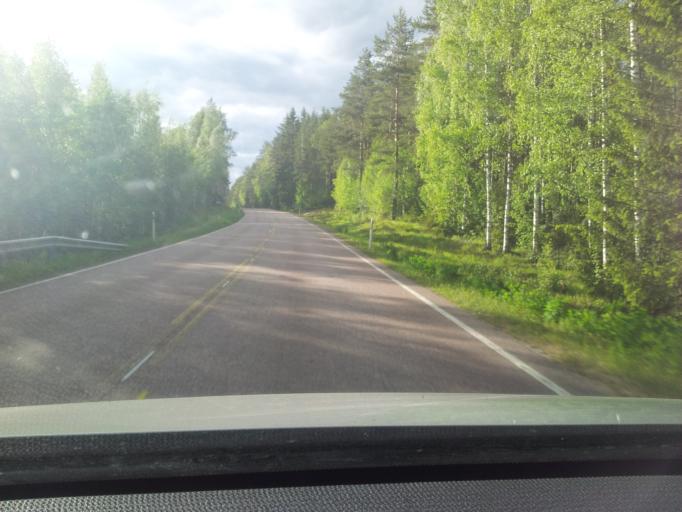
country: FI
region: South Karelia
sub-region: Lappeenranta
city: Luumaeki
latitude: 60.9628
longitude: 27.5722
